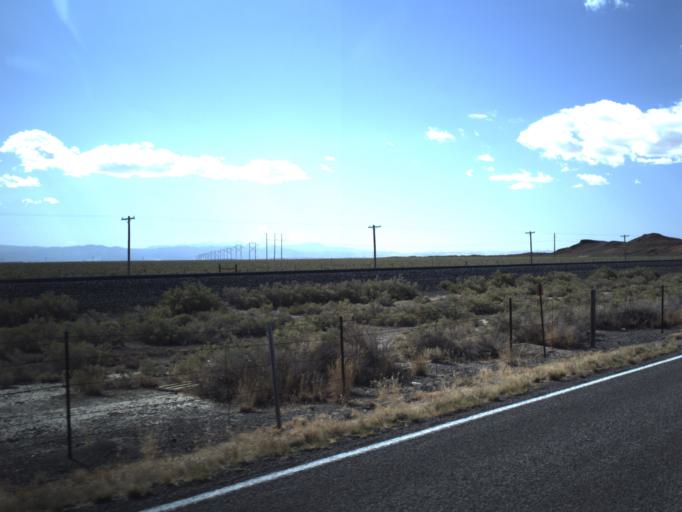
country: US
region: Utah
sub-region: Millard County
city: Delta
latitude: 39.1571
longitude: -112.7149
